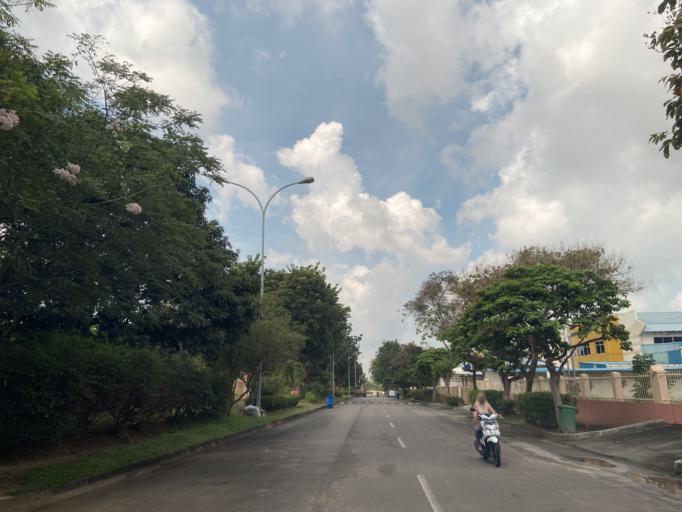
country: SG
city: Singapore
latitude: 1.1051
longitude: 104.0719
